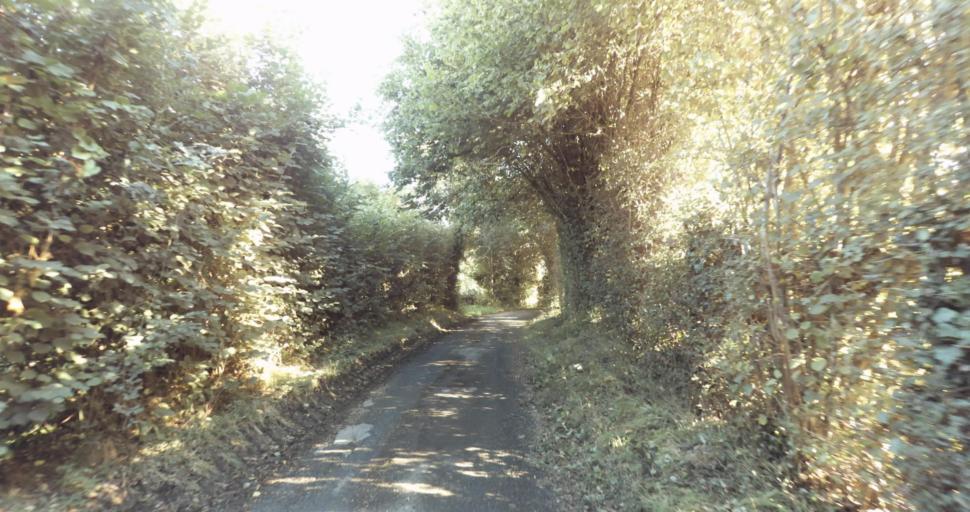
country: FR
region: Lower Normandy
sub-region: Departement de l'Orne
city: Vimoutiers
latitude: 48.8942
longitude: 0.1155
